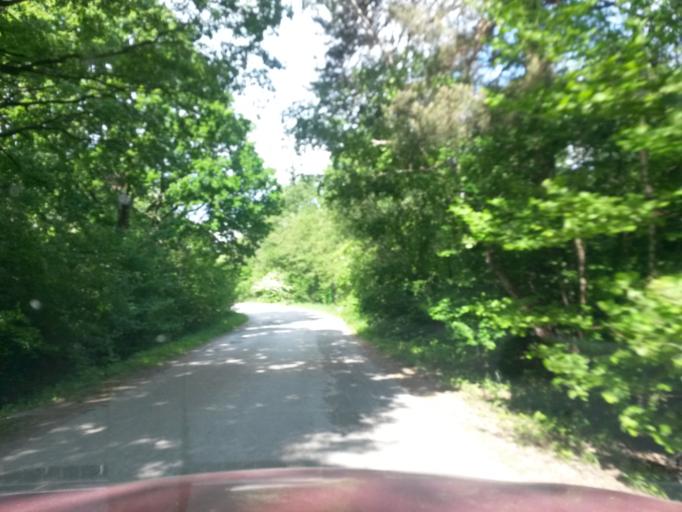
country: SK
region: Kosicky
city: Moldava nad Bodvou
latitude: 48.7106
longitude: 21.0188
